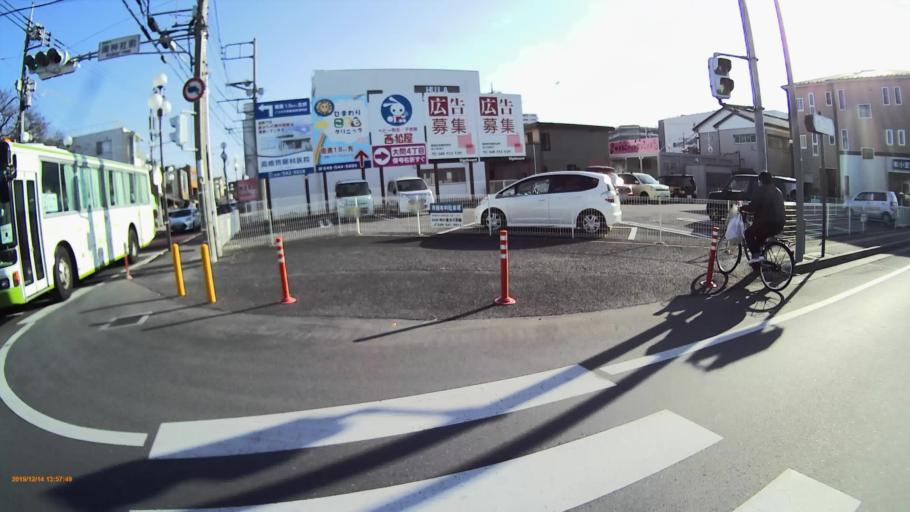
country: JP
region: Saitama
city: Konosu
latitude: 36.0627
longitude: 139.5099
